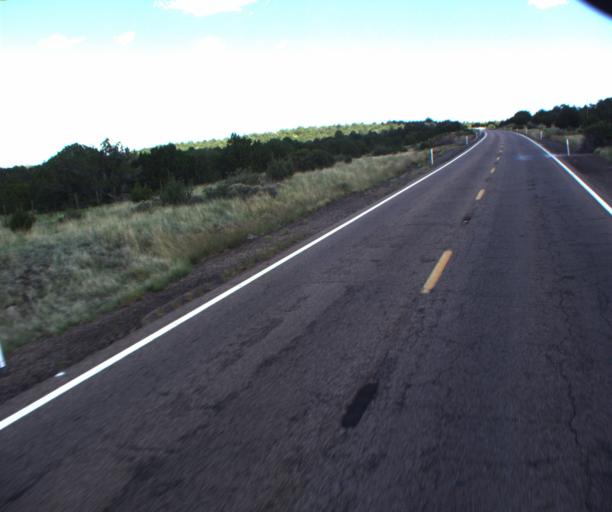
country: US
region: Arizona
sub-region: Apache County
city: Saint Johns
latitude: 34.2670
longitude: -109.6163
